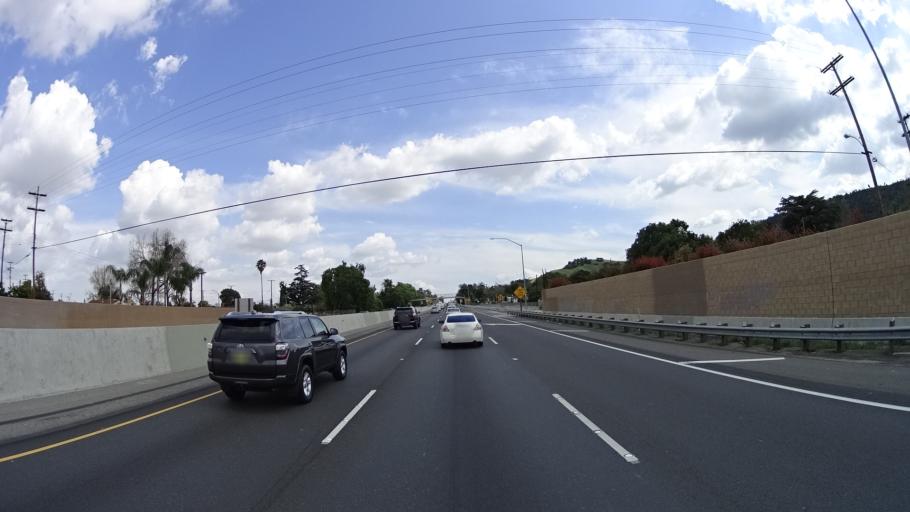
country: US
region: California
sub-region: Los Angeles County
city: Pomona
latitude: 34.0508
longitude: -117.7786
